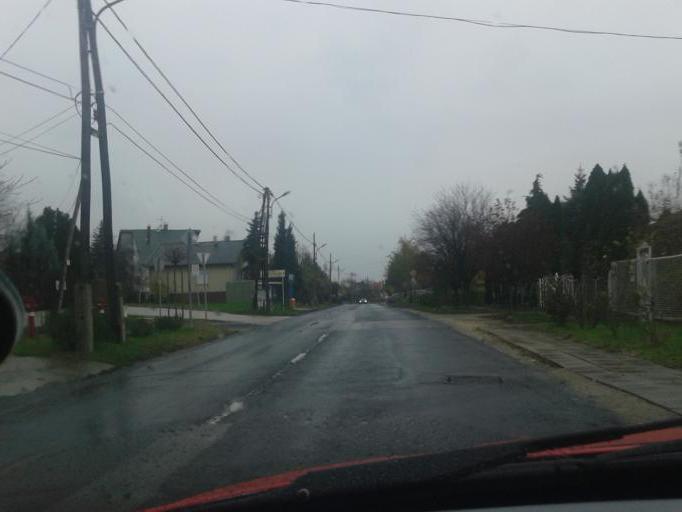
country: HU
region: Budapest
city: Budapest XXII. keruelet
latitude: 47.4286
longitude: 19.0080
